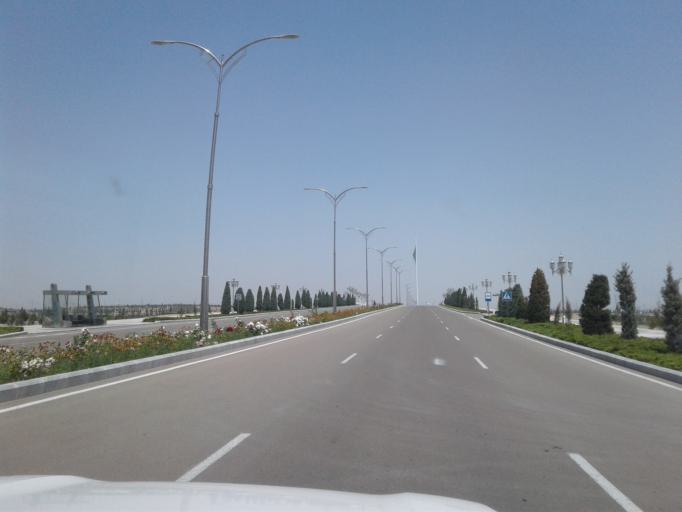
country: TM
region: Balkan
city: Turkmenbasy
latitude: 39.9538
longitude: 52.8568
